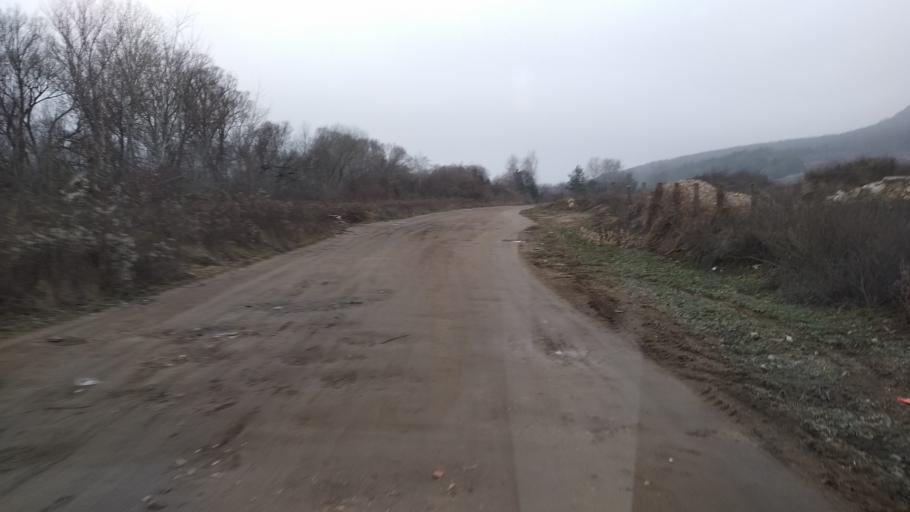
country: HU
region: Pest
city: Pilisborosjeno
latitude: 47.6012
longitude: 18.9693
